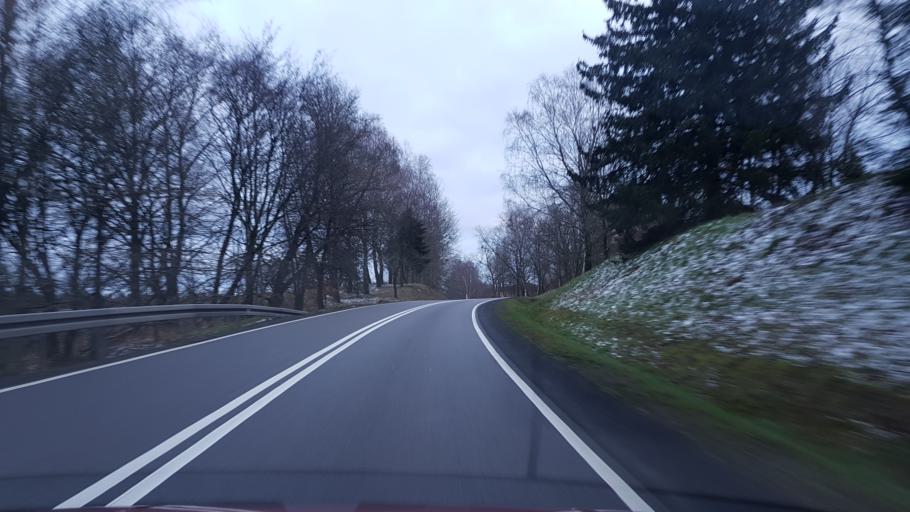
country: PL
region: Pomeranian Voivodeship
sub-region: Powiat bytowski
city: Tuchomie
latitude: 54.0503
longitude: 17.2130
